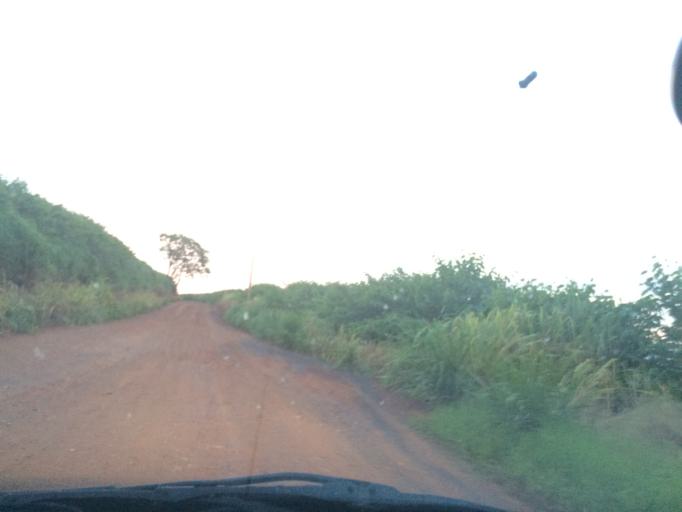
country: BR
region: Sao Paulo
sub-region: Tambau
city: Tambau
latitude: -21.6998
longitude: -47.2159
